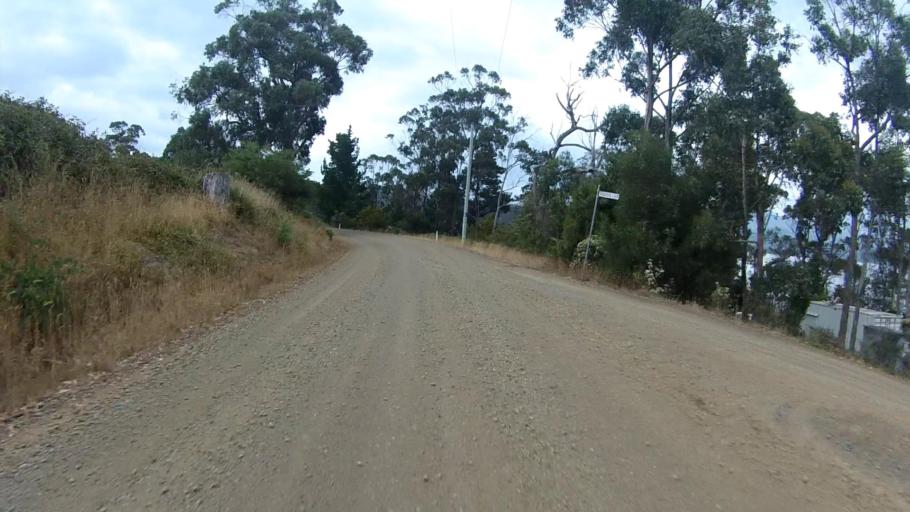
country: AU
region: Tasmania
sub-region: Huon Valley
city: Cygnet
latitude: -43.2355
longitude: 147.0989
